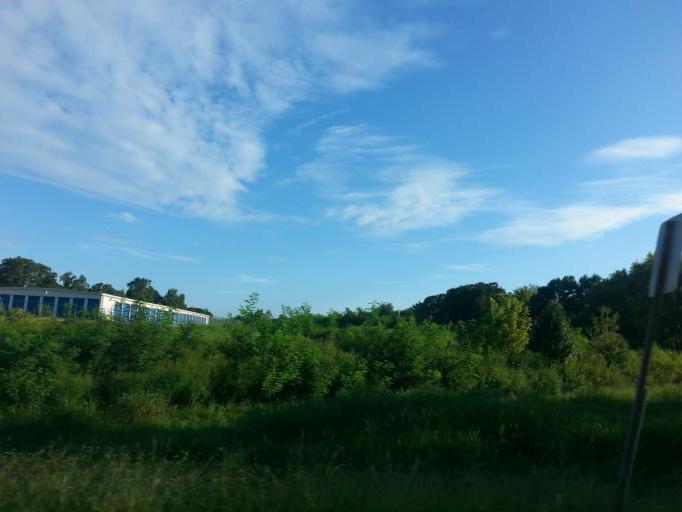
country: US
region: Alabama
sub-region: Lauderdale County
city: Killen
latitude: 34.8615
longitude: -87.4517
